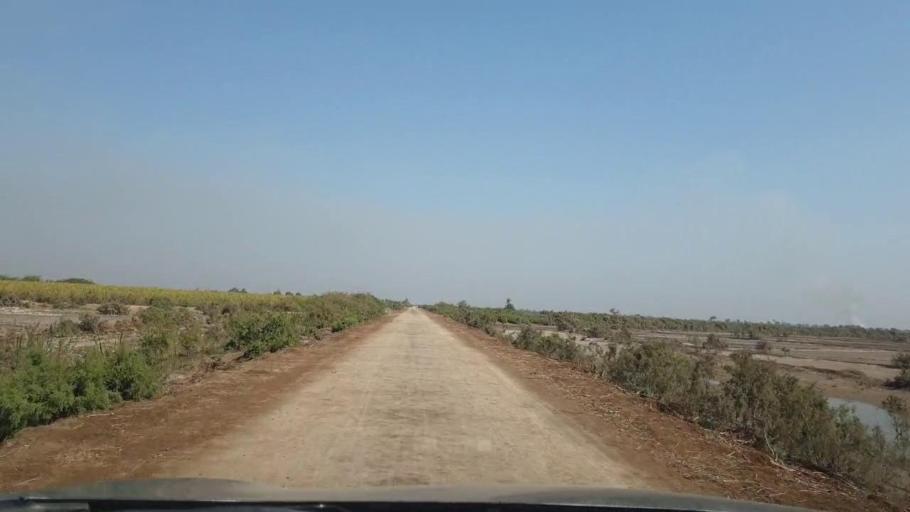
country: PK
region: Sindh
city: Berani
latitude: 25.6460
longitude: 68.8746
